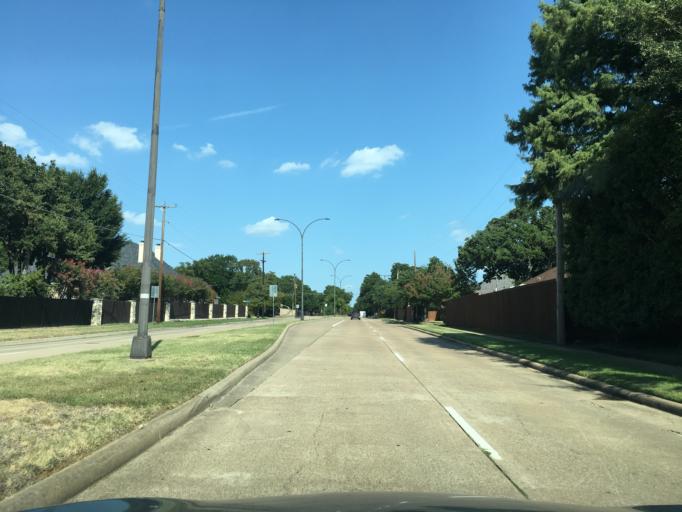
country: US
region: Texas
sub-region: Tarrant County
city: Dalworthington Gardens
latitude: 32.6703
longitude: -97.1478
